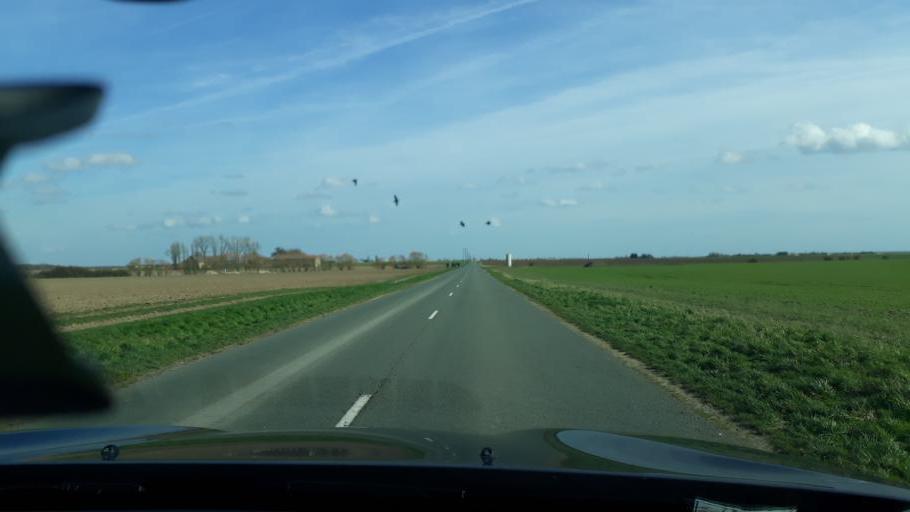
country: FR
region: Centre
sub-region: Departement du Loiret
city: Artenay
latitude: 48.0814
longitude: 1.9166
